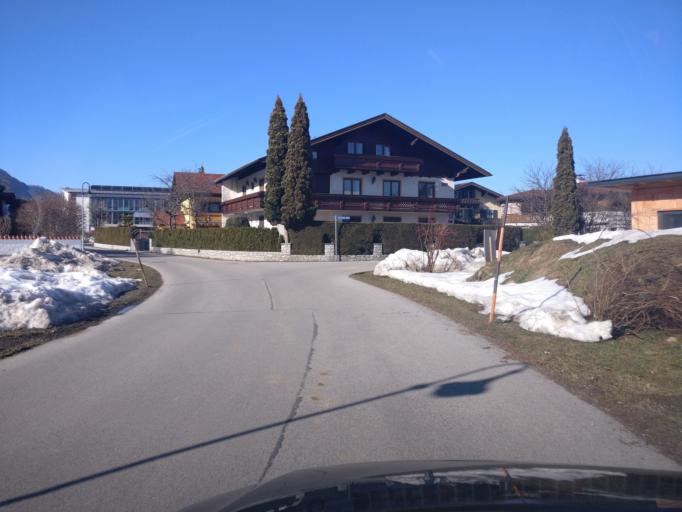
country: AT
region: Salzburg
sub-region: Politischer Bezirk Hallein
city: Kuchl
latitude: 47.6236
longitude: 13.1473
